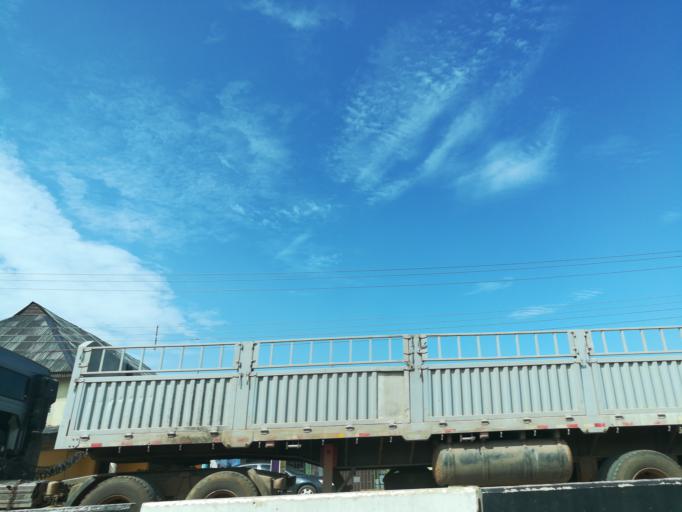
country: NG
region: Lagos
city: Ebute Ikorodu
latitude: 6.5952
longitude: 3.5042
